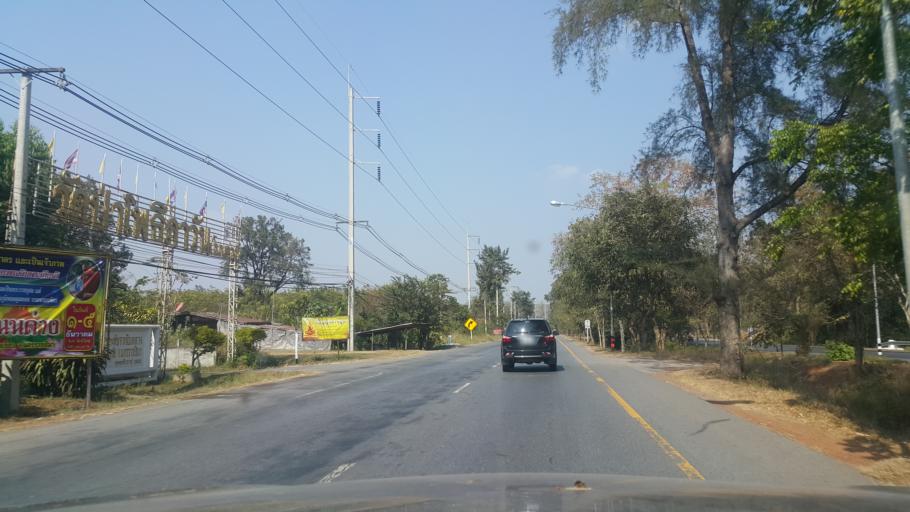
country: TH
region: Nakhon Ratchasima
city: Pak Thong Chai
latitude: 14.5626
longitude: 101.9771
